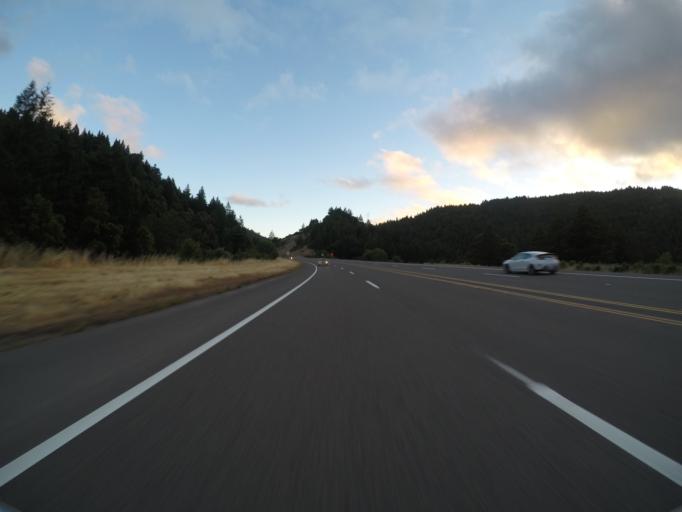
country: US
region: California
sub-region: Humboldt County
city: Redway
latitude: 39.9983
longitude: -123.7868
